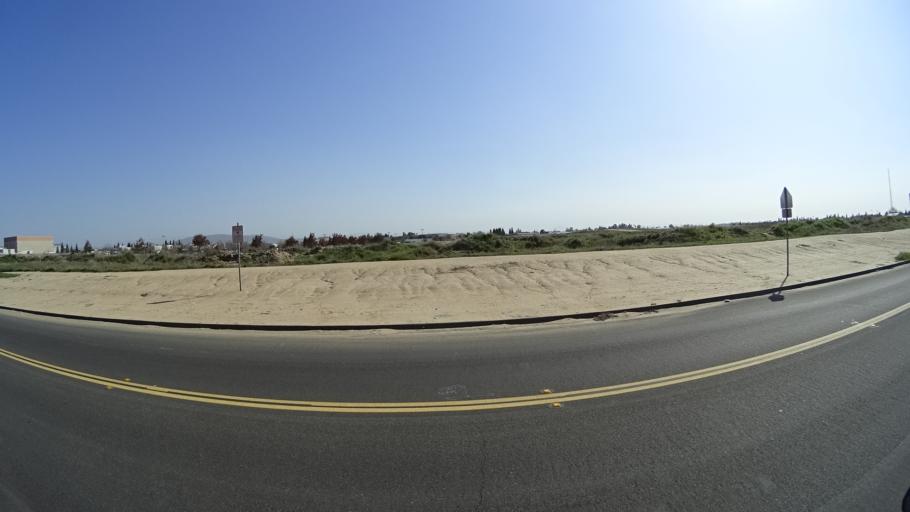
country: US
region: California
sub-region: Fresno County
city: Clovis
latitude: 36.8868
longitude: -119.7388
